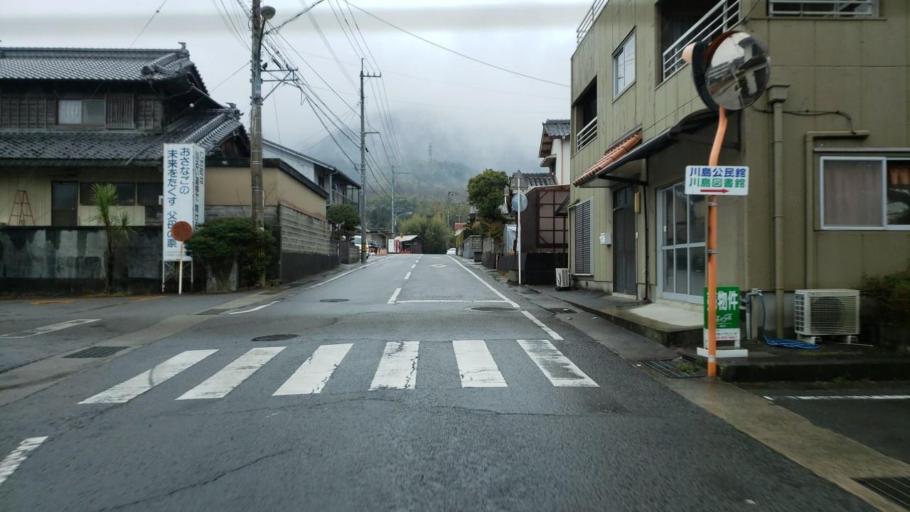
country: JP
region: Tokushima
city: Kamojimacho-jogejima
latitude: 34.0602
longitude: 134.3191
